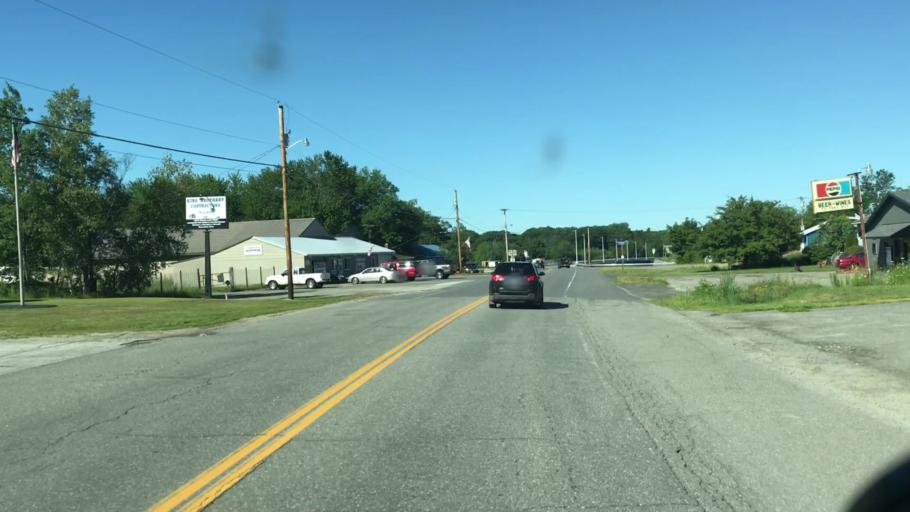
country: US
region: Maine
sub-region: Penobscot County
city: Howland
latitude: 45.2377
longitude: -68.6474
